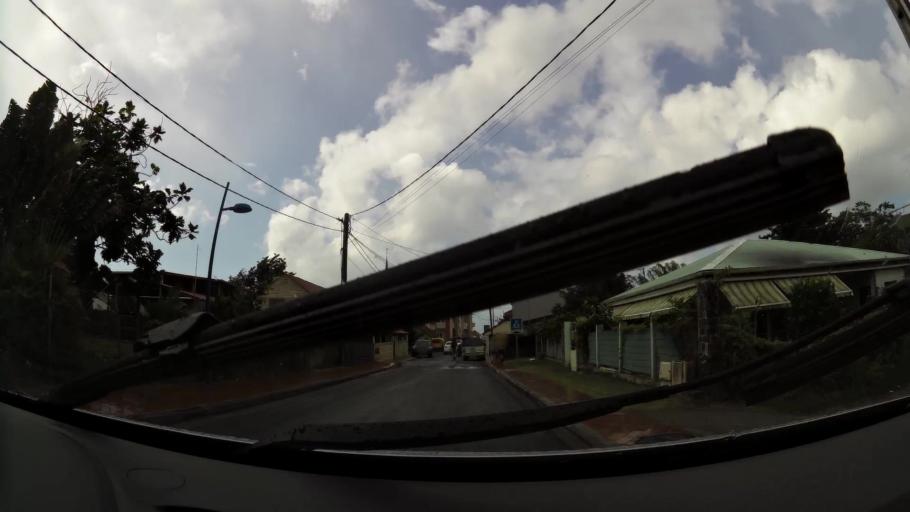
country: MQ
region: Martinique
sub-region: Martinique
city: Les Trois-Ilets
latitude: 14.4918
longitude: -61.0796
